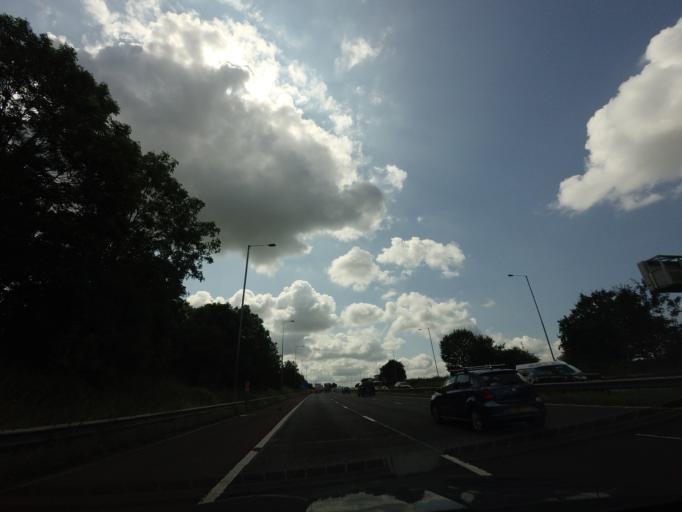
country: GB
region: England
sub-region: Lancashire
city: Euxton
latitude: 53.6504
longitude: -2.6911
